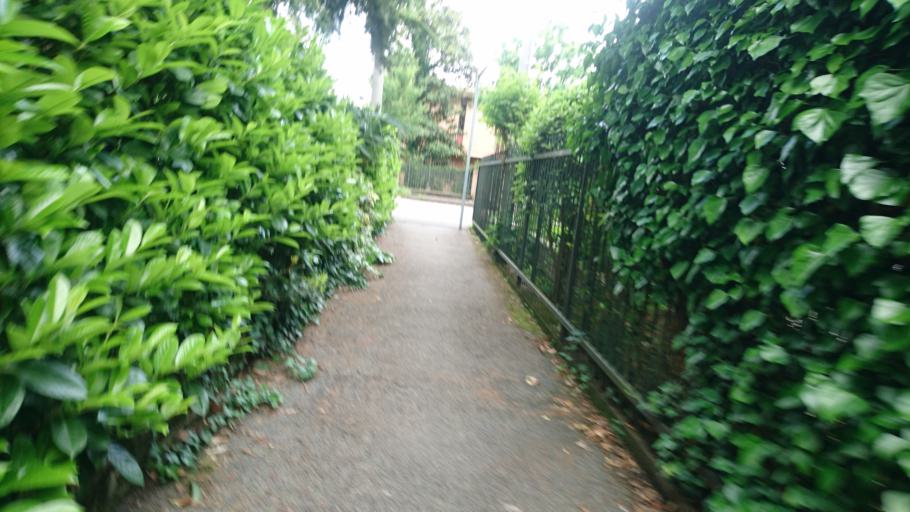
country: IT
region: Veneto
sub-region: Provincia di Padova
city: Mandriola-Sant'Agostino
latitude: 45.3836
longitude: 11.8535
